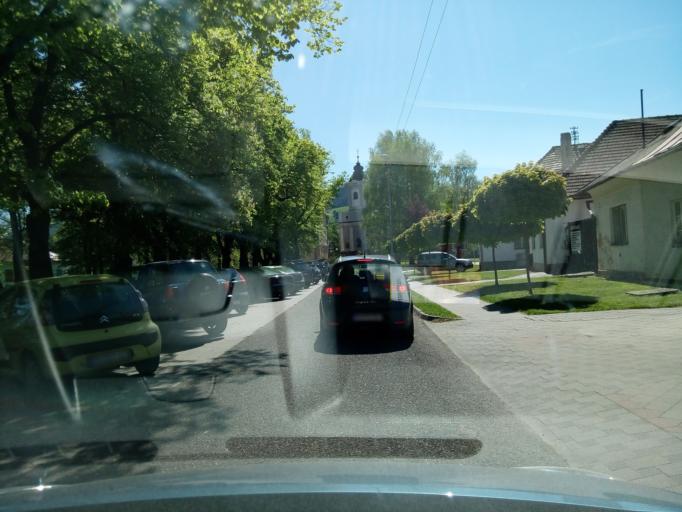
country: SK
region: Zilinsky
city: Ruzomberok
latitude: 49.0806
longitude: 19.3008
